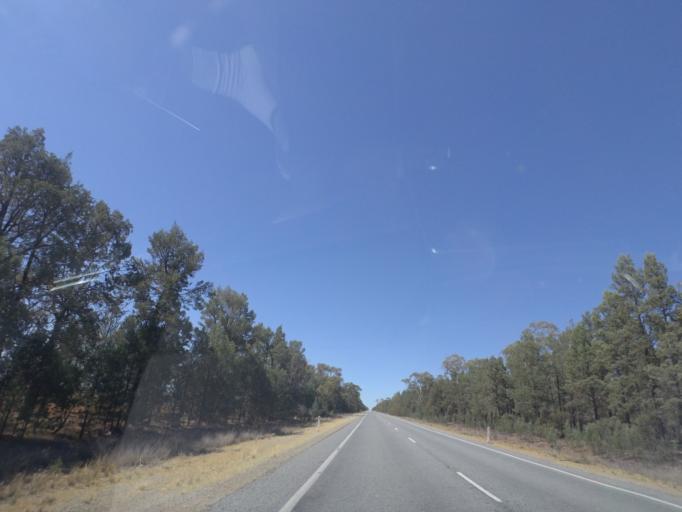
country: AU
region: New South Wales
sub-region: Narrandera
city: Narrandera
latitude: -34.4245
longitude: 146.8444
